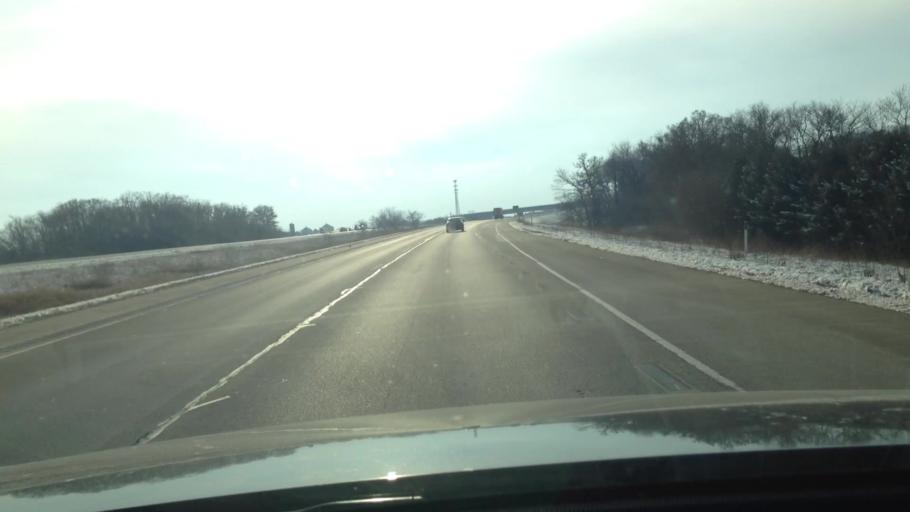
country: US
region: Wisconsin
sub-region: Walworth County
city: East Troy
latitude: 42.7528
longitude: -88.4393
